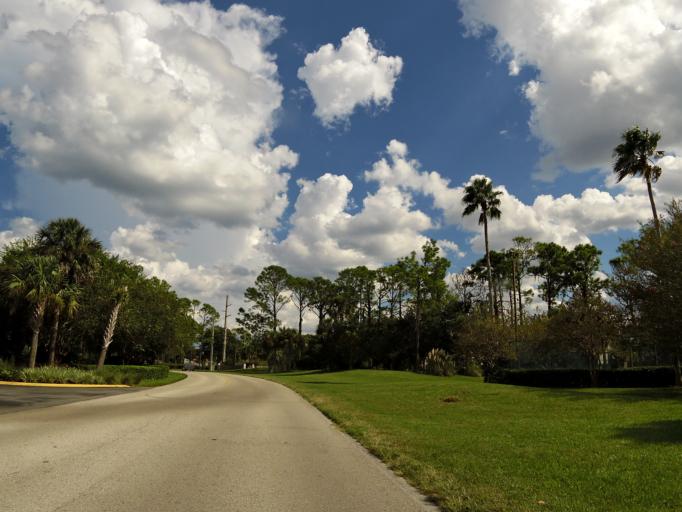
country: US
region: Florida
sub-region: Saint Johns County
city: Ponte Vedra Beach
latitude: 30.2497
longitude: -81.3954
